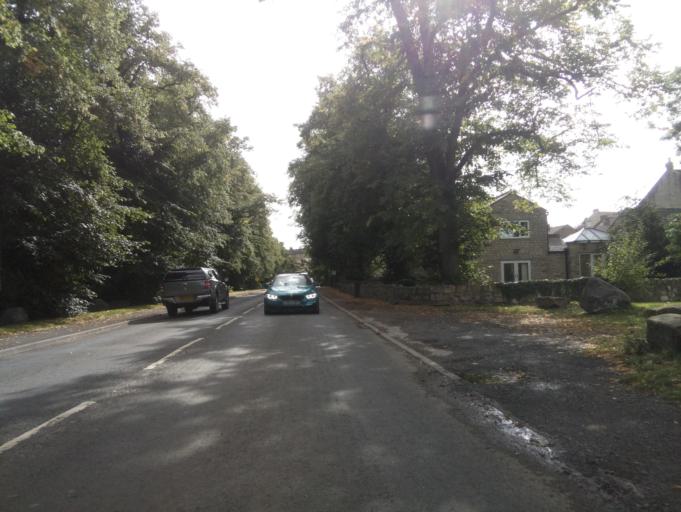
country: GB
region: England
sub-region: North Yorkshire
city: Bedale
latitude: 54.2252
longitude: -1.6561
